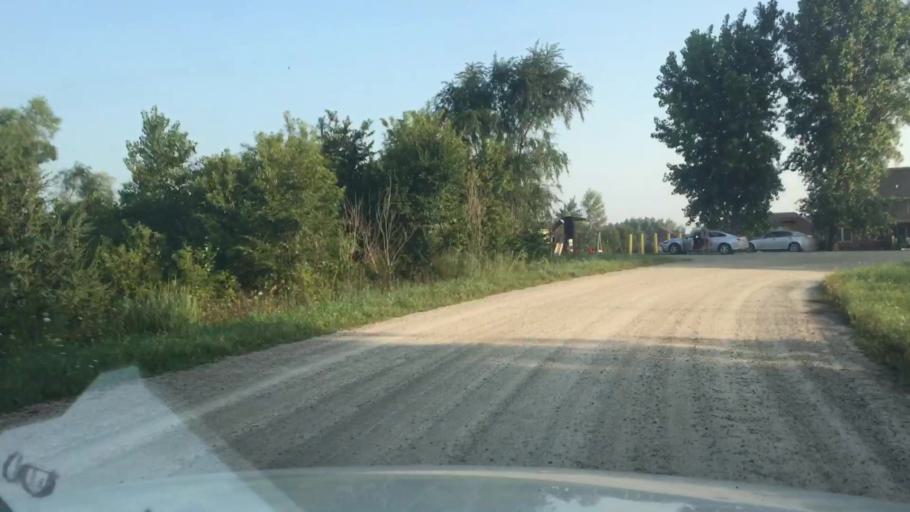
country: US
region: Iowa
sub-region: Story County
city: Huxley
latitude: 41.8925
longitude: -93.5820
